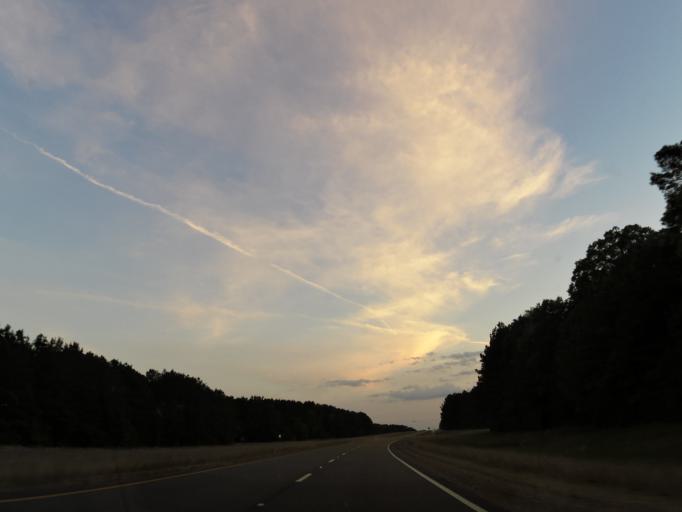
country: US
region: Mississippi
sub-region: Kemper County
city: De Kalb
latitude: 32.7333
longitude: -88.4681
